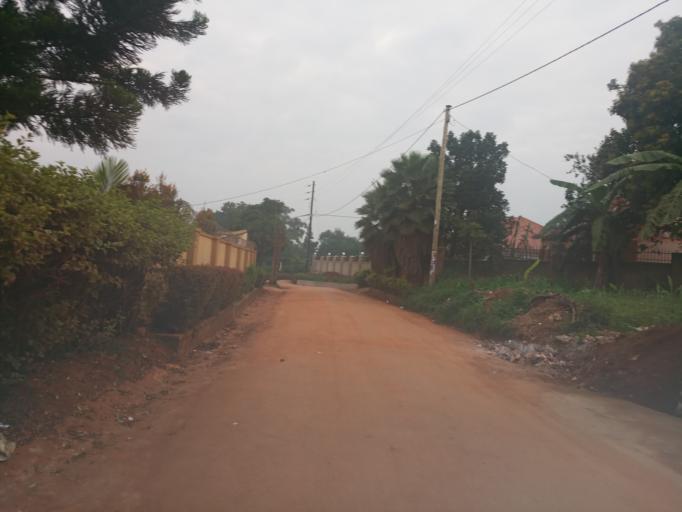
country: UG
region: Central Region
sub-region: Wakiso District
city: Kireka
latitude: 0.3929
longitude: 32.6349
